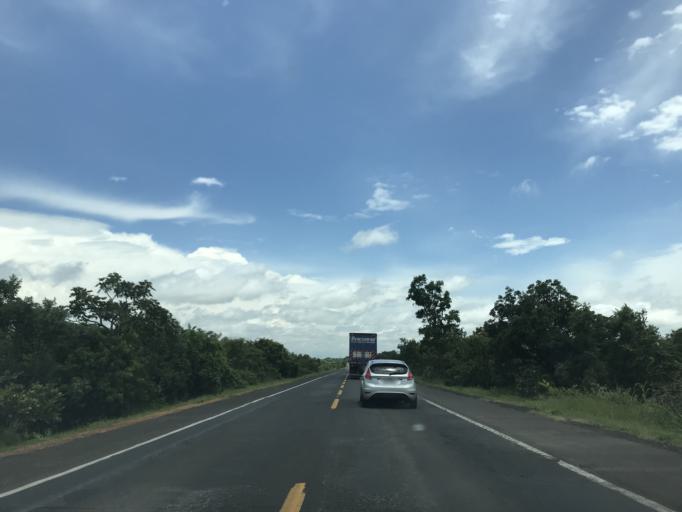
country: BR
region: Minas Gerais
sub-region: Prata
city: Prata
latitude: -19.6629
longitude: -48.9817
